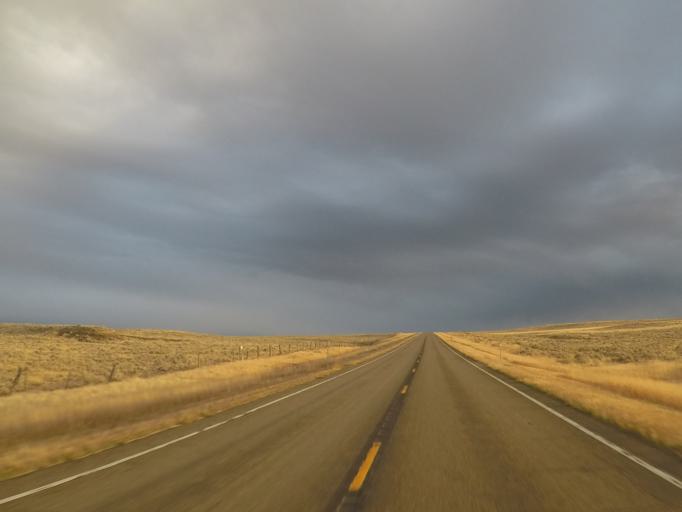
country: US
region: Montana
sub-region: Golden Valley County
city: Ryegate
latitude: 46.3203
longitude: -109.2575
